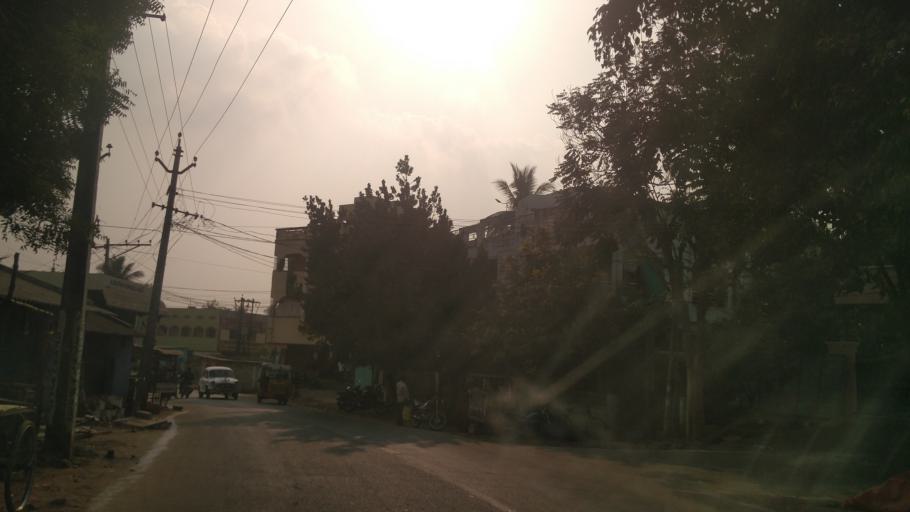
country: IN
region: Andhra Pradesh
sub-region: East Godavari
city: Rajahmundry
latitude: 16.9528
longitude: 81.7893
